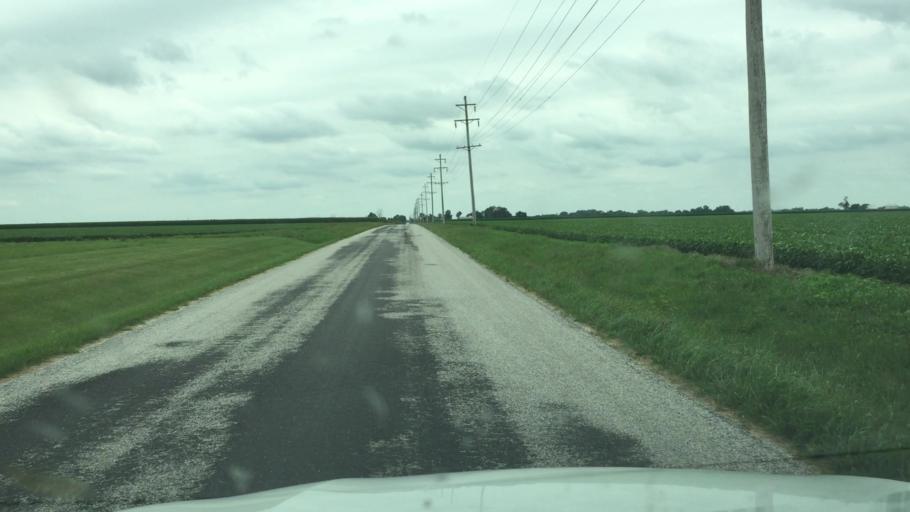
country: US
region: Illinois
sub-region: Hancock County
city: Carthage
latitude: 40.4000
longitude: -91.0825
